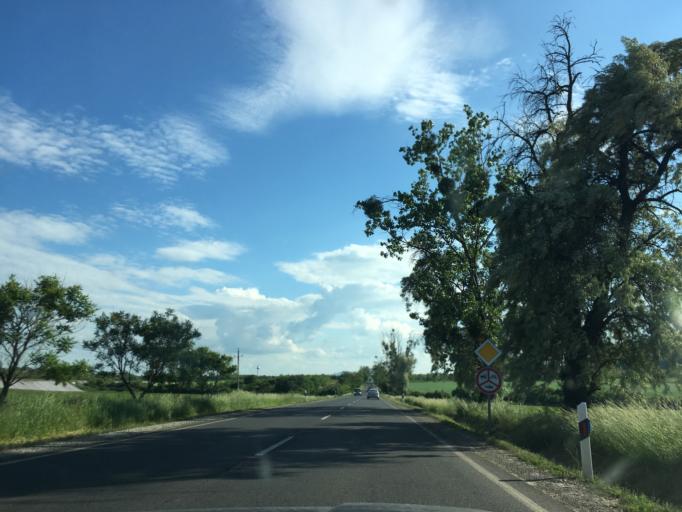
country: HU
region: Borsod-Abauj-Zemplen
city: Sarospatak
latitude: 48.2991
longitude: 21.5166
